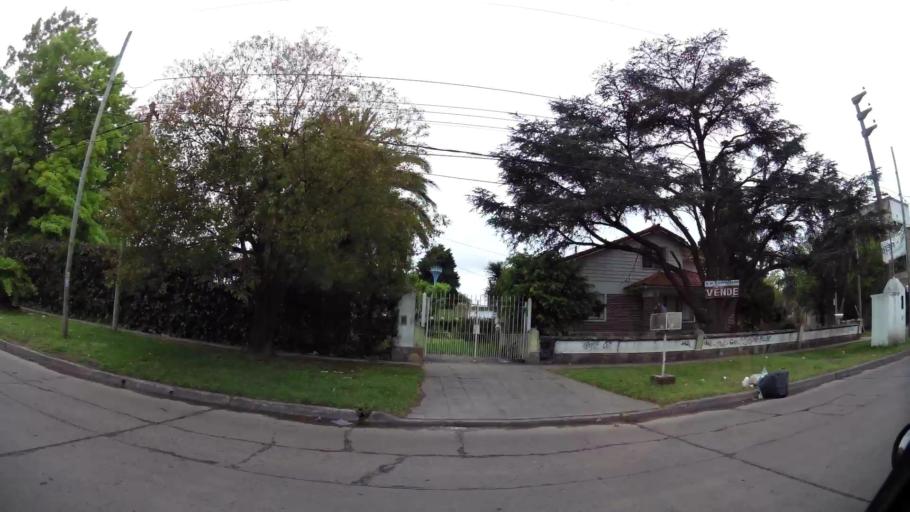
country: AR
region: Buenos Aires
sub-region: Partido de Quilmes
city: Quilmes
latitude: -34.7565
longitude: -58.2351
